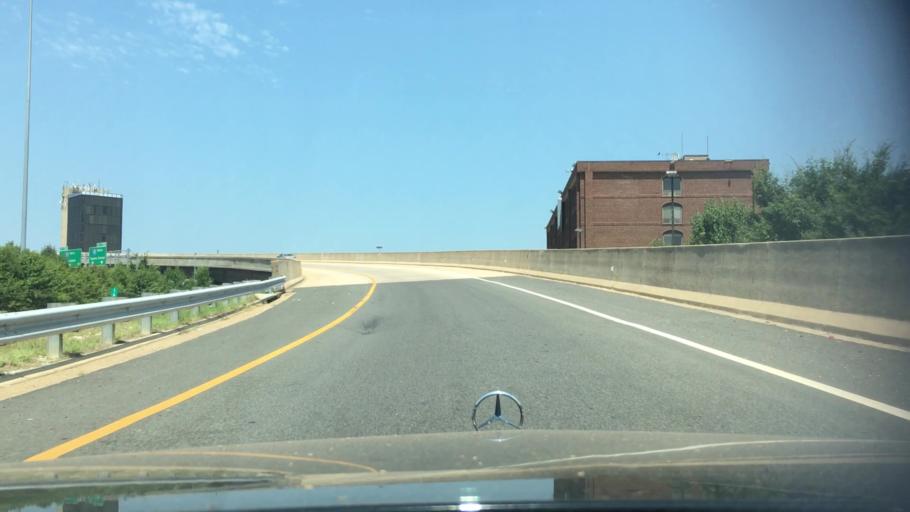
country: US
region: Virginia
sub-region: Fairfax County
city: Springfield
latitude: 38.7793
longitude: -77.1779
